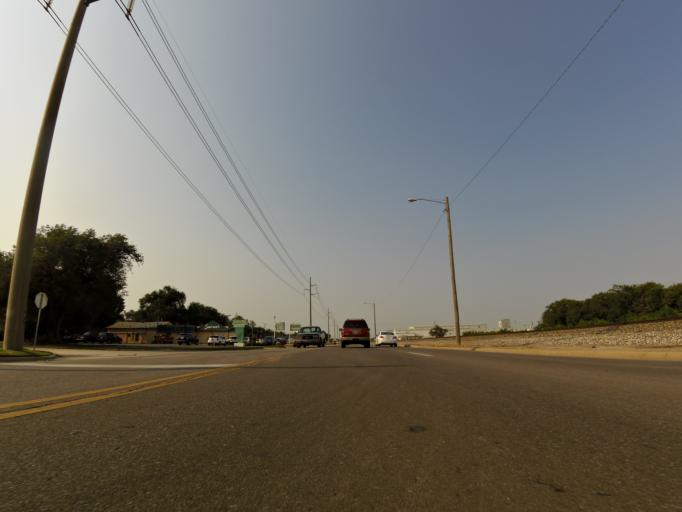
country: US
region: Kansas
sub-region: Sedgwick County
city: Wichita
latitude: 37.7426
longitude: -97.3360
